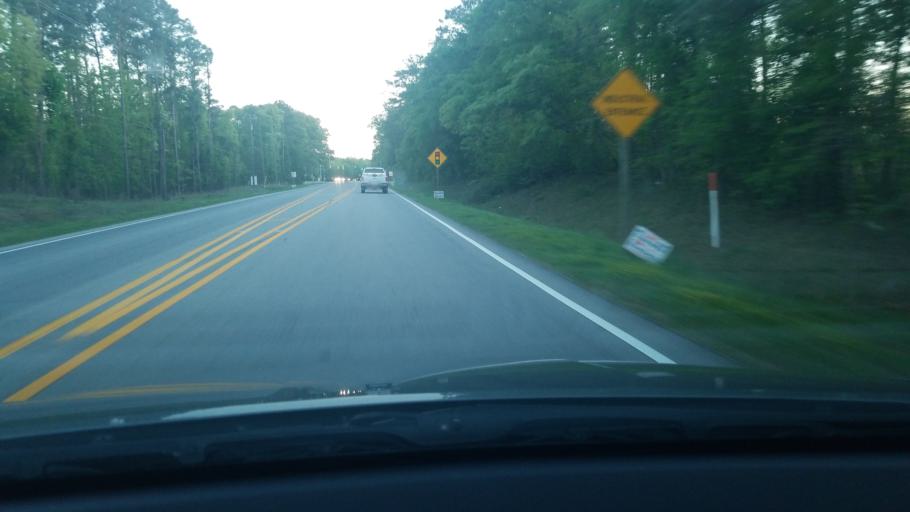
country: US
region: North Carolina
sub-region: Craven County
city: Vanceboro
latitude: 35.2192
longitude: -77.1202
